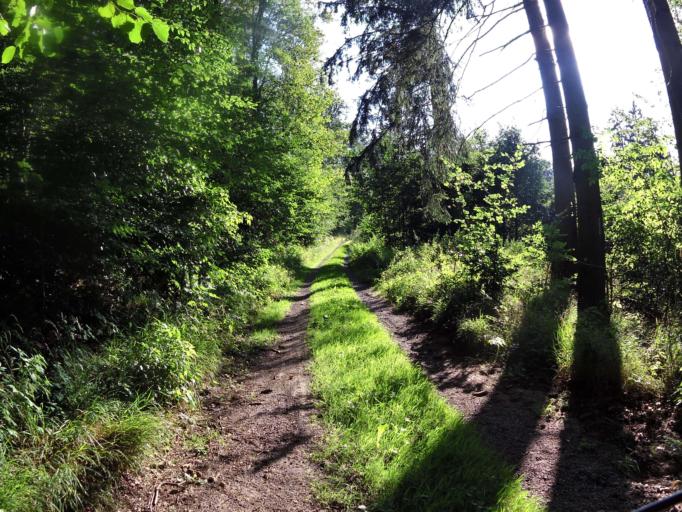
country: DE
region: Thuringia
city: Eisenach
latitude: 50.9557
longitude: 10.3478
